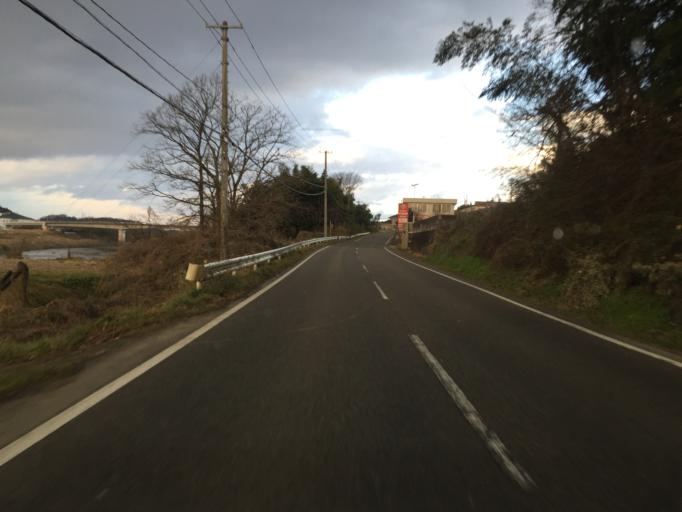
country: JP
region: Fukushima
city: Nihommatsu
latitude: 37.5797
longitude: 140.4509
